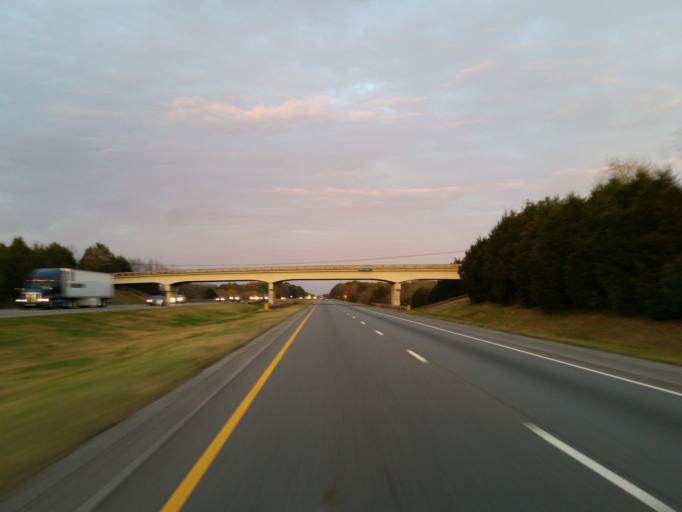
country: US
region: Alabama
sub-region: Sumter County
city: Livingston
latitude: 32.7137
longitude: -88.1282
